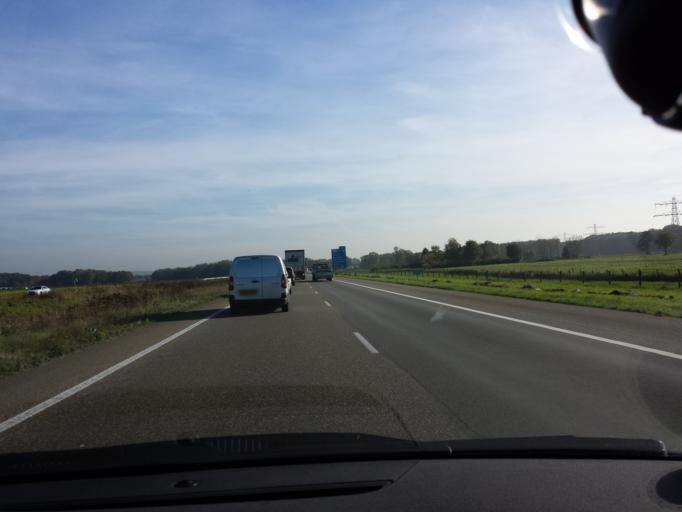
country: NL
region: Gelderland
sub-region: Gemeente Nijmegen
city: Lindenholt
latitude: 51.7858
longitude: 5.8221
